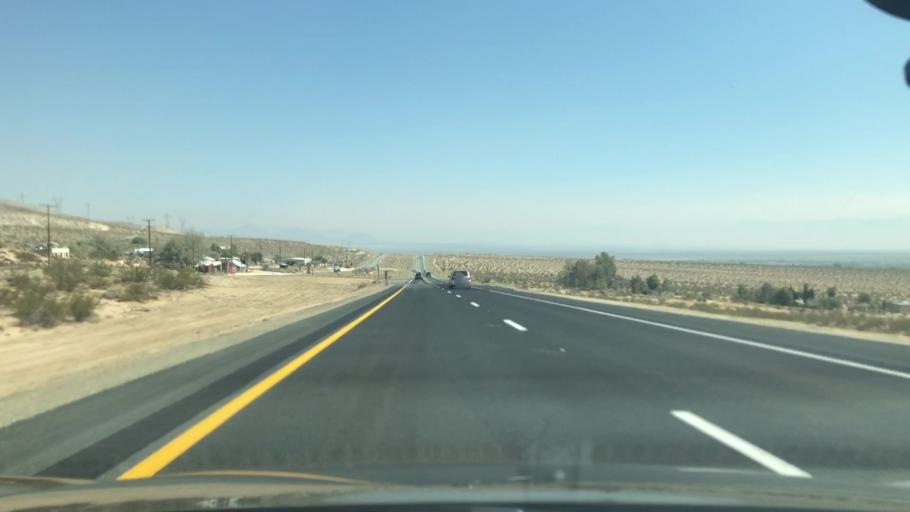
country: US
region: California
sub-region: Kern County
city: Inyokern
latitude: 35.6617
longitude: -117.8739
